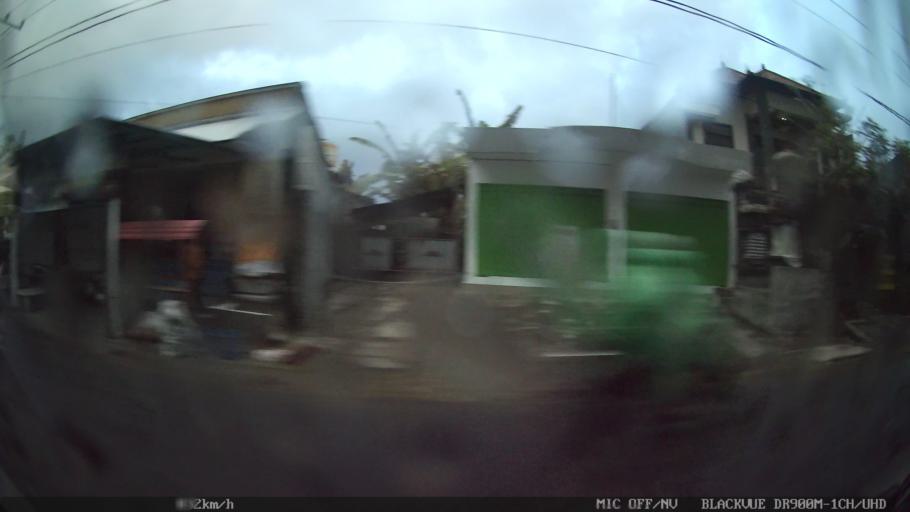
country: ID
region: Bali
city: Banjar Batur
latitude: -8.6026
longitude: 115.2200
